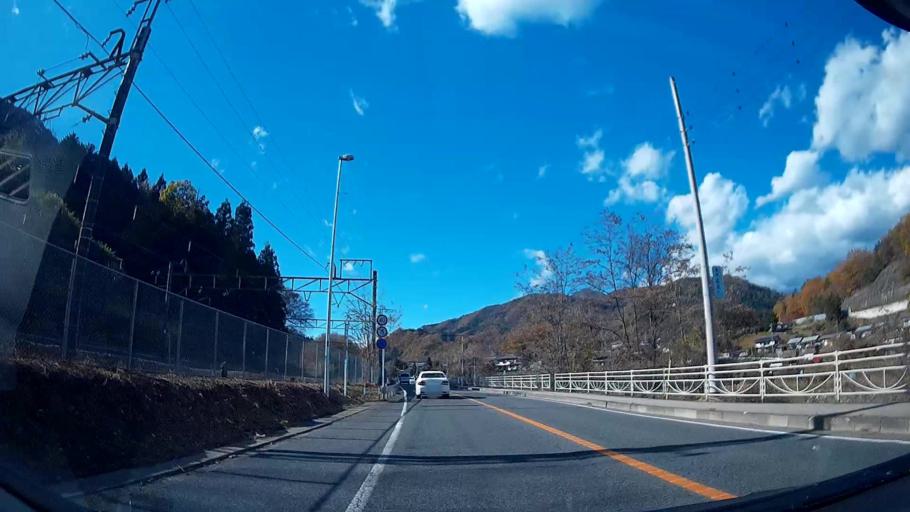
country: JP
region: Yamanashi
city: Otsuki
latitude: 35.6001
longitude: 138.9084
